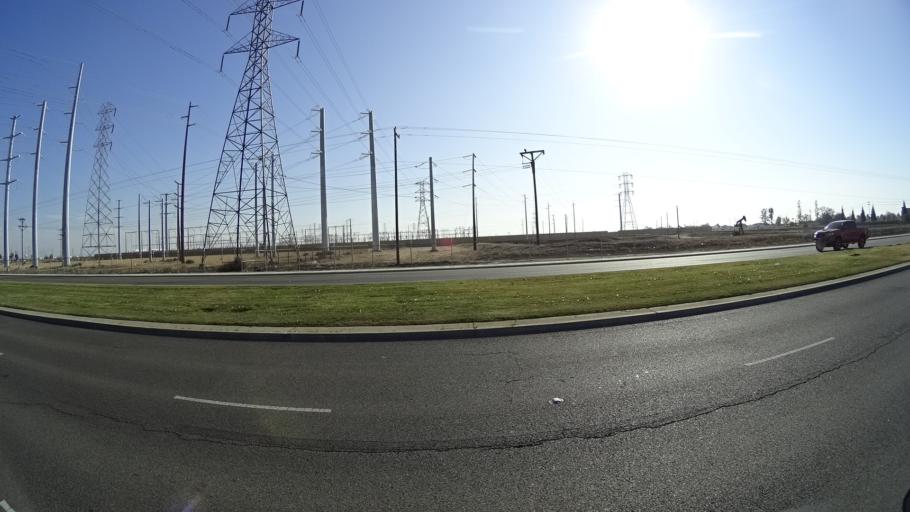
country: US
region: California
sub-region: Kern County
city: Greenacres
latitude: 35.3835
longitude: -119.0981
